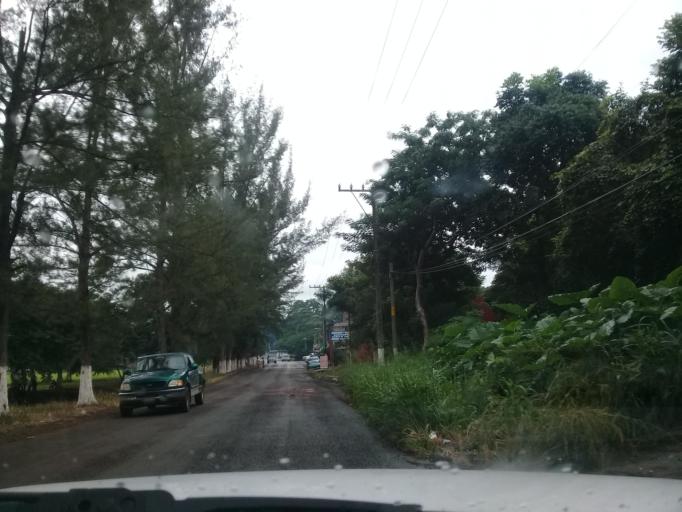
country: MX
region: Veracruz
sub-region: San Andres Tuxtla
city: Cerro las Iguanas
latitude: 18.4253
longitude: -95.2170
